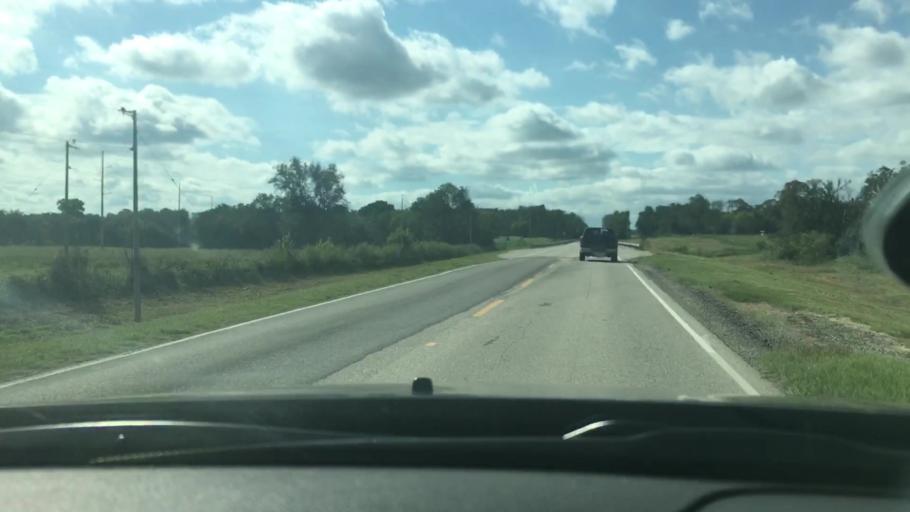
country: US
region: Oklahoma
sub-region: Pontotoc County
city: Ada
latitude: 34.7057
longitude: -96.6349
